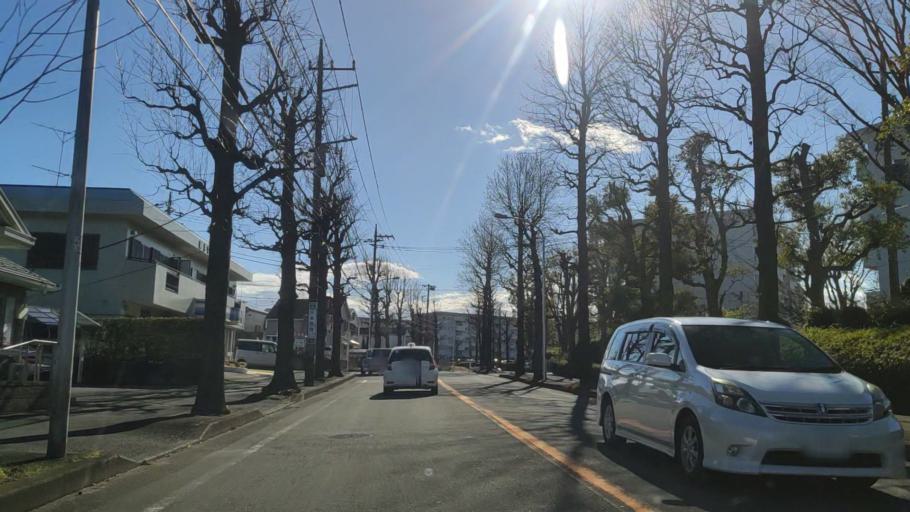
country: JP
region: Tokyo
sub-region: Machida-shi
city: Machida
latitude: 35.5158
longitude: 139.5079
